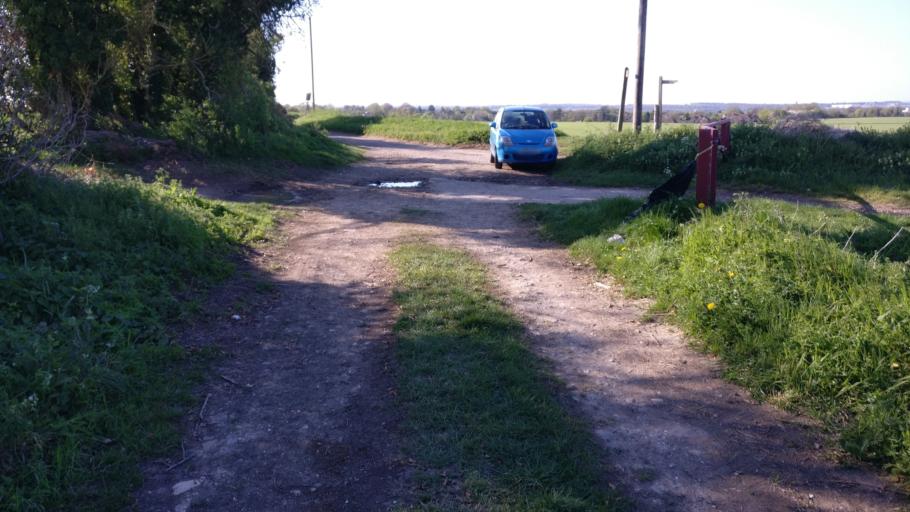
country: GB
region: England
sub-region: Hampshire
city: Basingstoke
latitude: 51.2326
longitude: -1.0892
